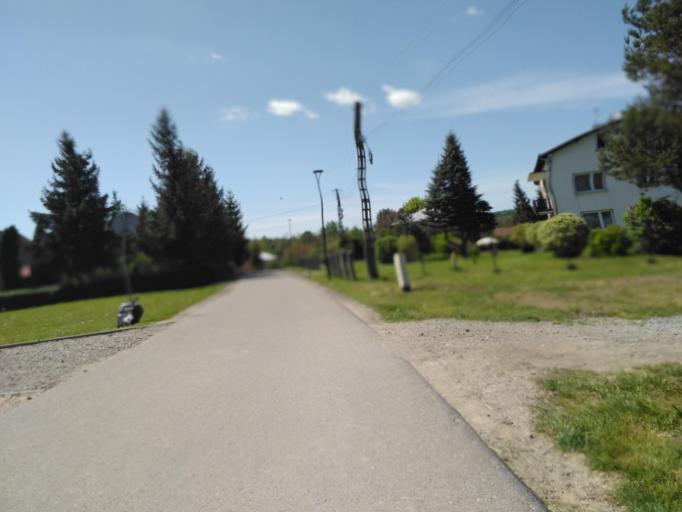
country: PL
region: Subcarpathian Voivodeship
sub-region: Powiat krosnienski
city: Miejsce Piastowe
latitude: 49.6174
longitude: 21.7625
